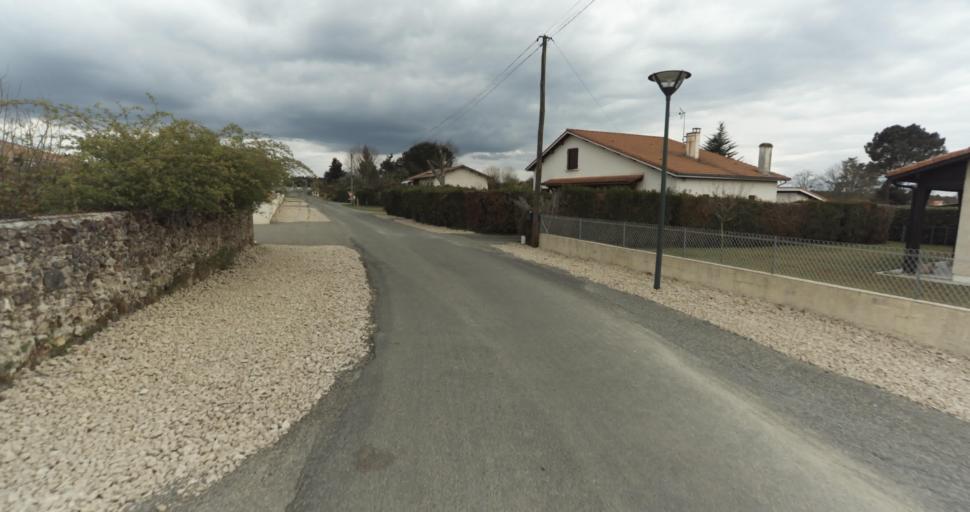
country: FR
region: Aquitaine
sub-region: Departement des Landes
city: Roquefort
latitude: 44.0265
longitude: -0.3290
